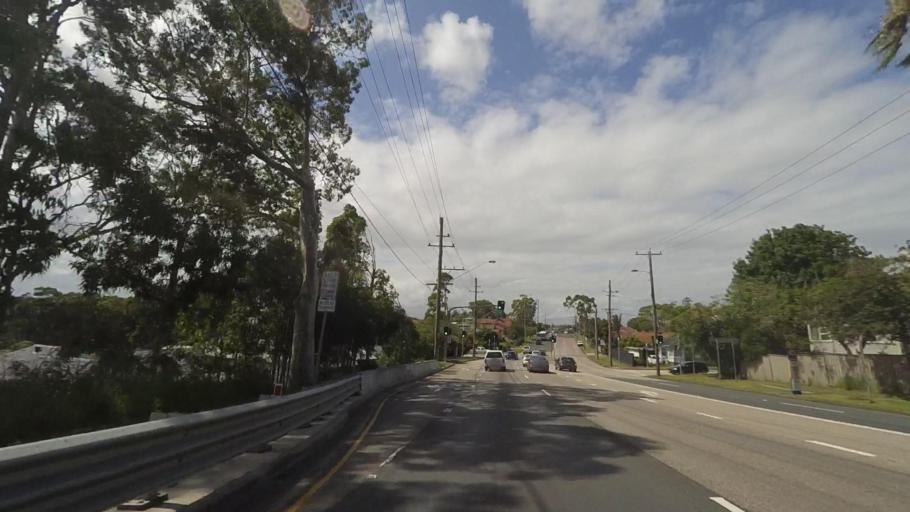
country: AU
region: New South Wales
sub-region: Newcastle
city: Lambton
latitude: -32.9176
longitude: 151.7034
